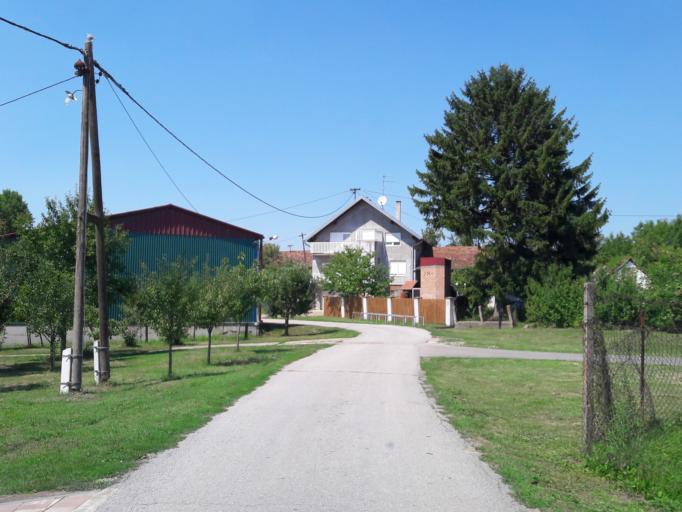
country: HR
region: Vukovarsko-Srijemska
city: Vodinci
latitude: 45.2836
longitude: 18.5615
